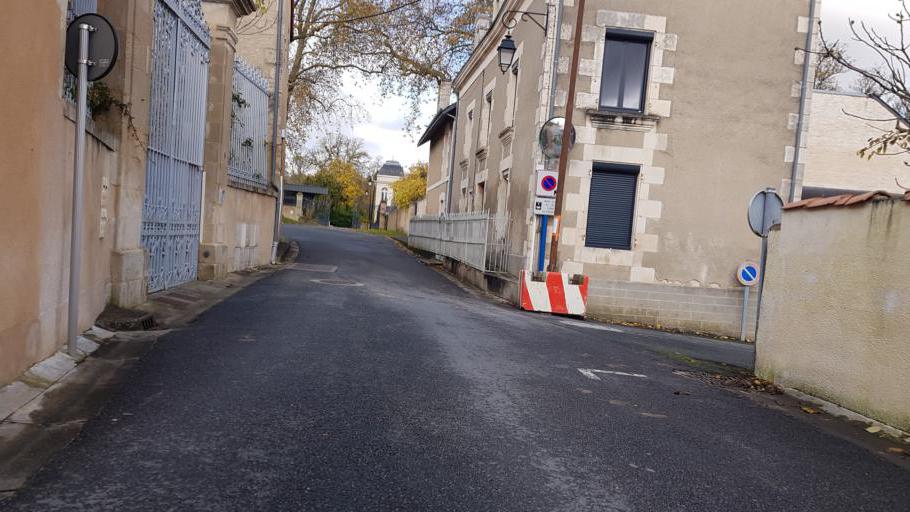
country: FR
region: Poitou-Charentes
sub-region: Departement de la Vienne
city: Chasseneuil-du-Poitou
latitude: 46.6503
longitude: 0.3757
